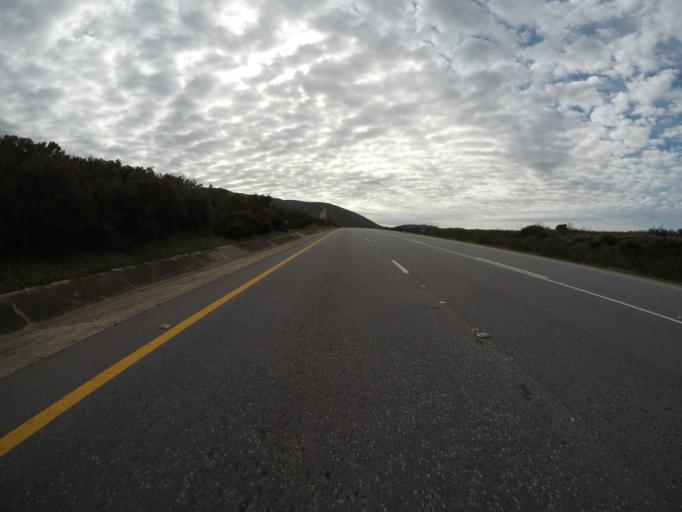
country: ZA
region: Eastern Cape
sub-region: Cacadu District Municipality
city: Kruisfontein
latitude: -34.0011
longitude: 24.6825
